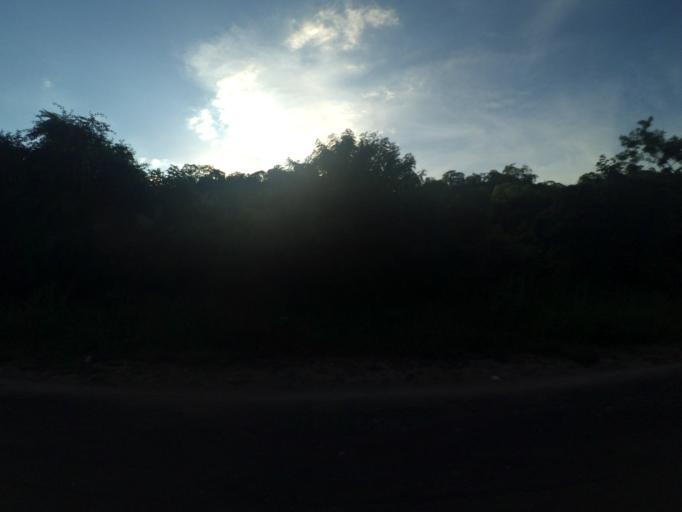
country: BO
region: Santa Cruz
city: Abapo
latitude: -18.8717
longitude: -63.3747
